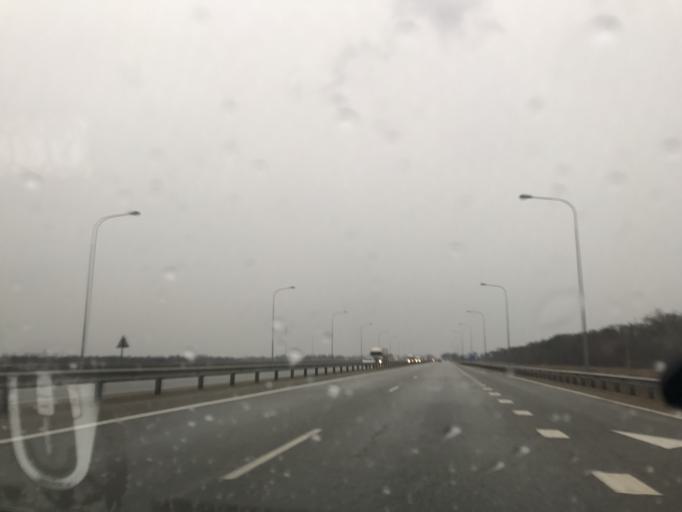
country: RU
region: Krasnodarskiy
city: Pavlovskaya
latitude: 46.2680
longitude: 39.8316
